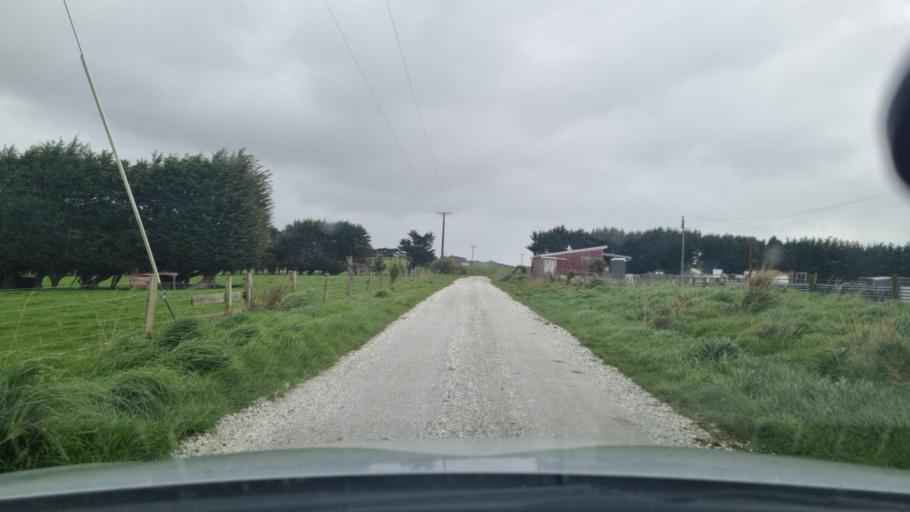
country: NZ
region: Southland
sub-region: Invercargill City
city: Bluff
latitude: -46.5415
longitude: 168.2923
